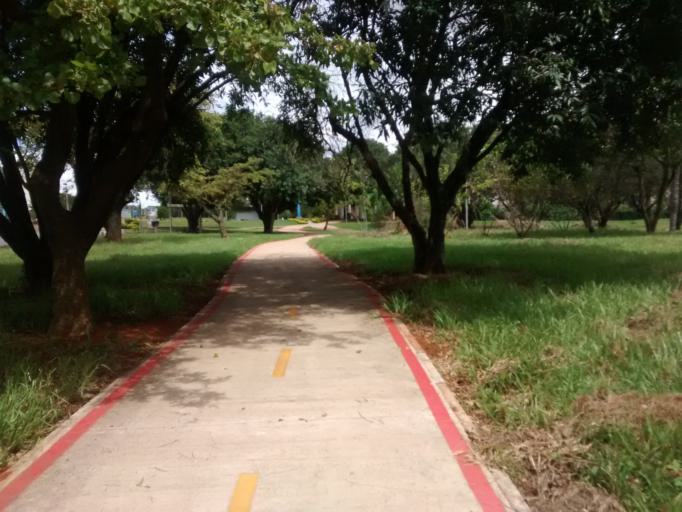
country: BR
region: Federal District
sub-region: Brasilia
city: Brasilia
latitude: -15.7648
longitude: -47.8660
